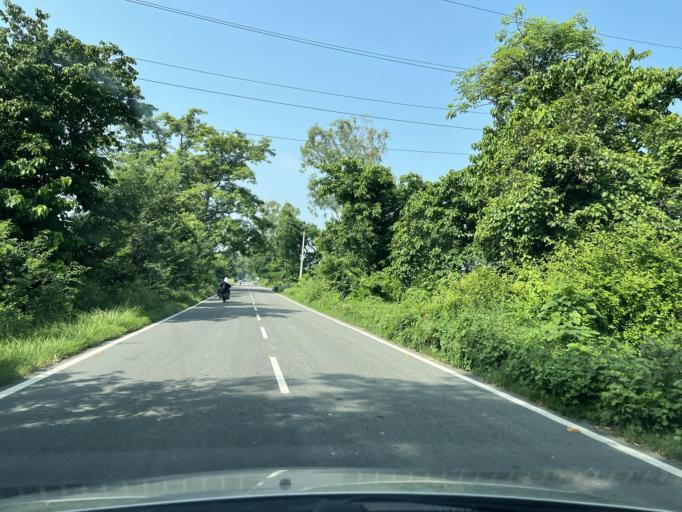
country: IN
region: Uttarakhand
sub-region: Udham Singh Nagar
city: Bazpur
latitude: 29.1940
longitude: 79.1952
